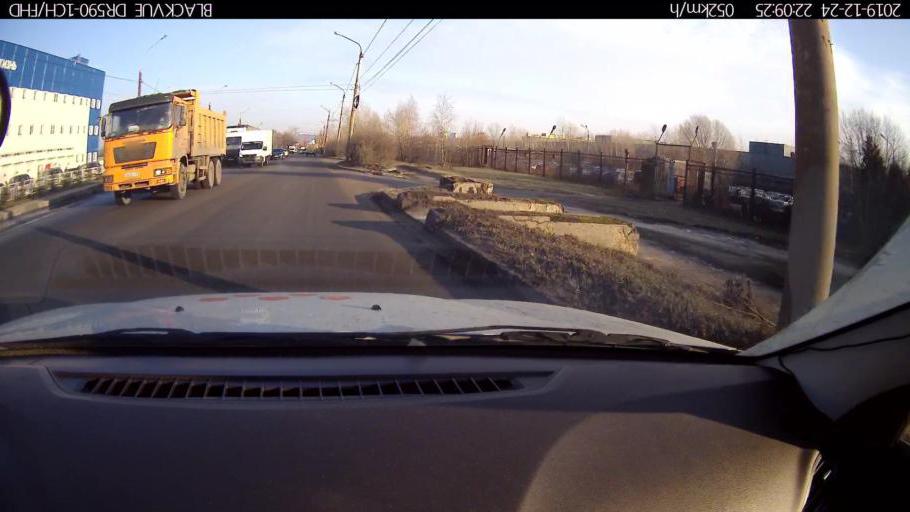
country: RU
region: Nizjnij Novgorod
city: Nizhniy Novgorod
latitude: 56.2536
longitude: 43.9230
